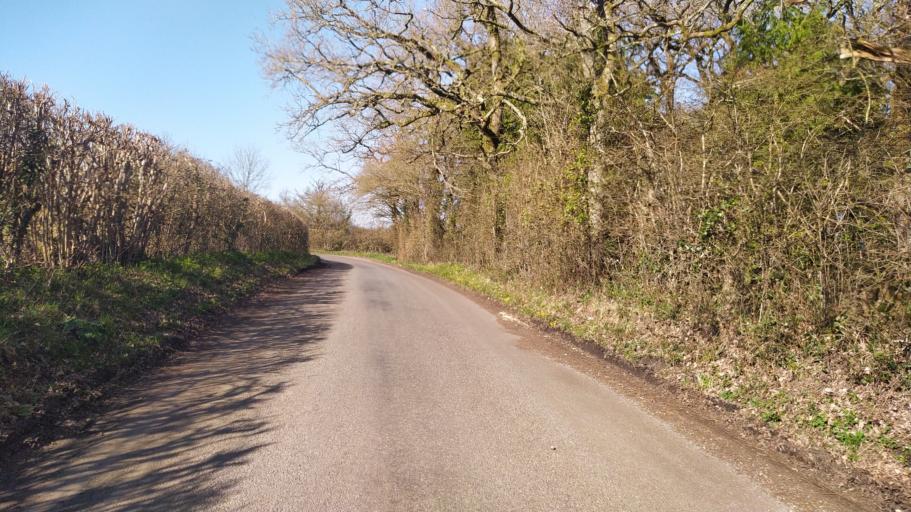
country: GB
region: England
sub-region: Dorset
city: Verwood
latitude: 50.8962
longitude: -1.9111
